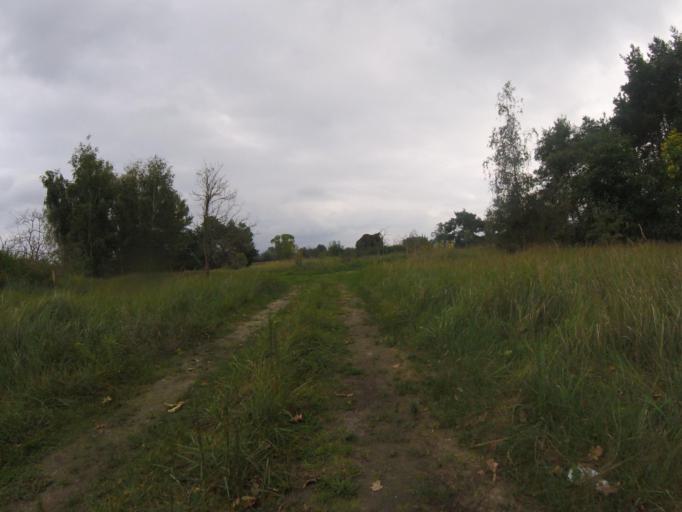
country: DE
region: Brandenburg
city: Mittenwalde
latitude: 52.2549
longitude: 13.5151
